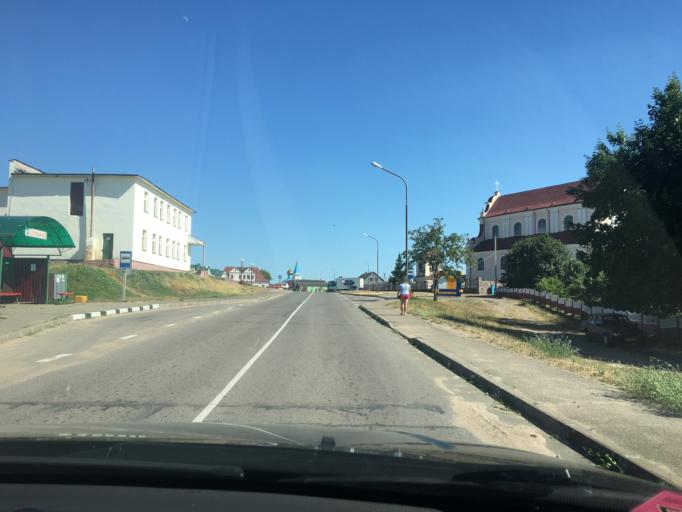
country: BY
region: Grodnenskaya
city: Hal'shany
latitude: 54.2581
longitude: 26.0092
